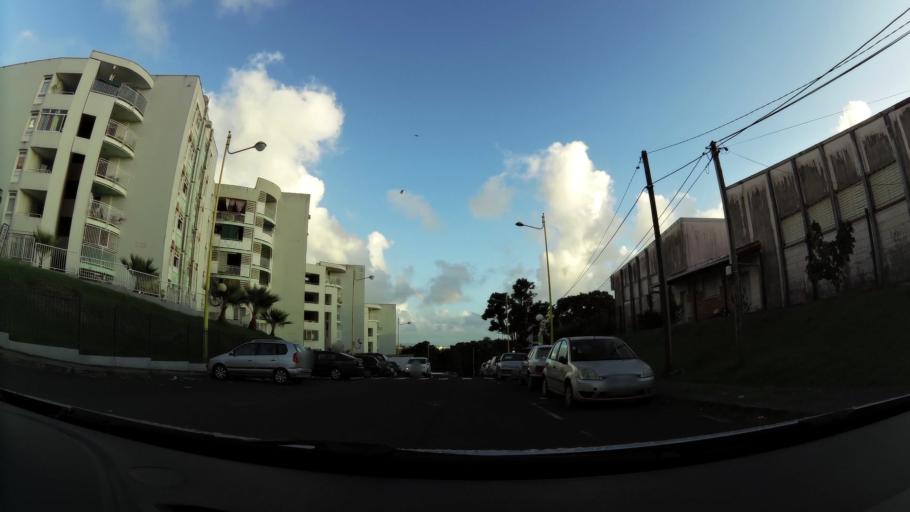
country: MQ
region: Martinique
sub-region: Martinique
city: Fort-de-France
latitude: 14.6340
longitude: -61.0686
